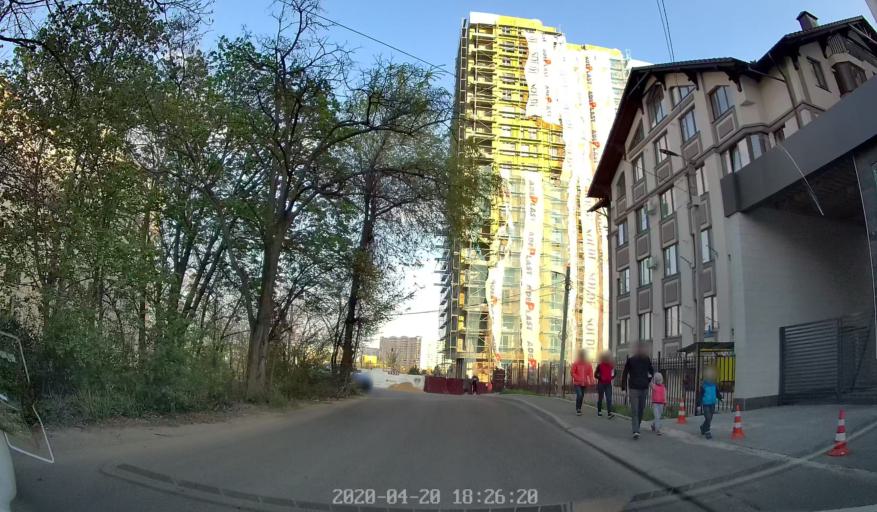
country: MD
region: Chisinau
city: Chisinau
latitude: 46.9921
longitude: 28.8374
